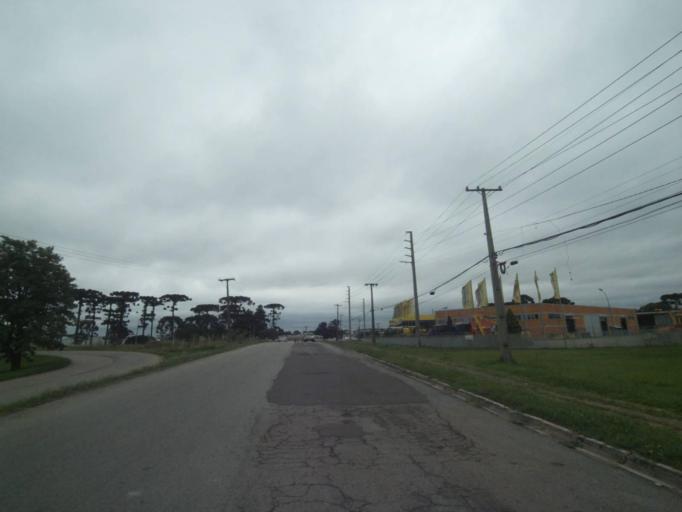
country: BR
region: Parana
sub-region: Araucaria
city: Araucaria
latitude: -25.5228
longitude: -49.3307
